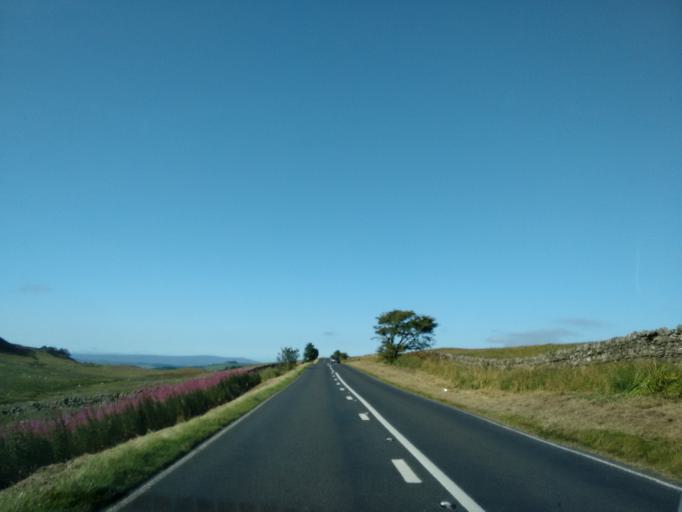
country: GB
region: England
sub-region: Northumberland
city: Bardon Mill
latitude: 55.0069
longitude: -2.3333
